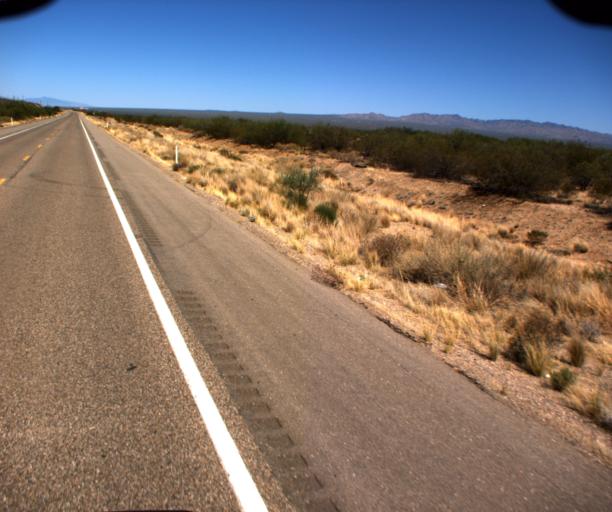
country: US
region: Arizona
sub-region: Pima County
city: Three Points
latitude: 32.0412
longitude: -111.4530
